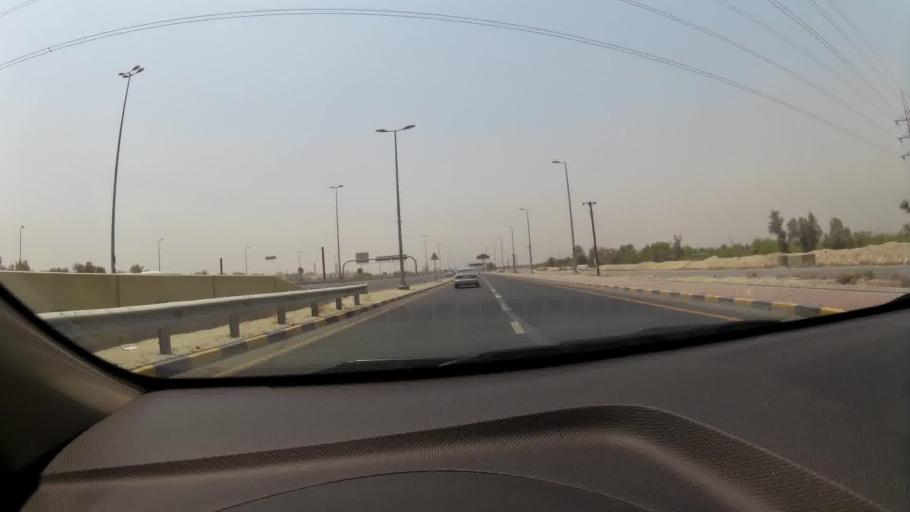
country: KW
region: Al Asimah
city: Ar Rabiyah
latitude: 29.3118
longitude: 47.8011
